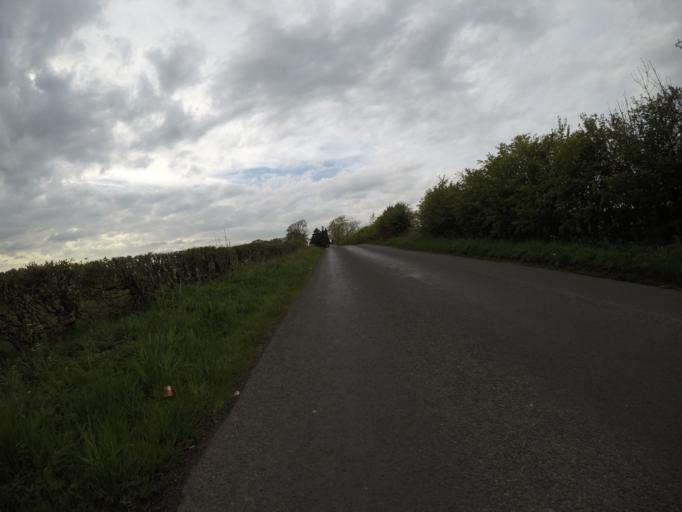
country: GB
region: Scotland
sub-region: East Ayrshire
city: Kilmarnock
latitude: 55.6450
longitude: -4.4835
